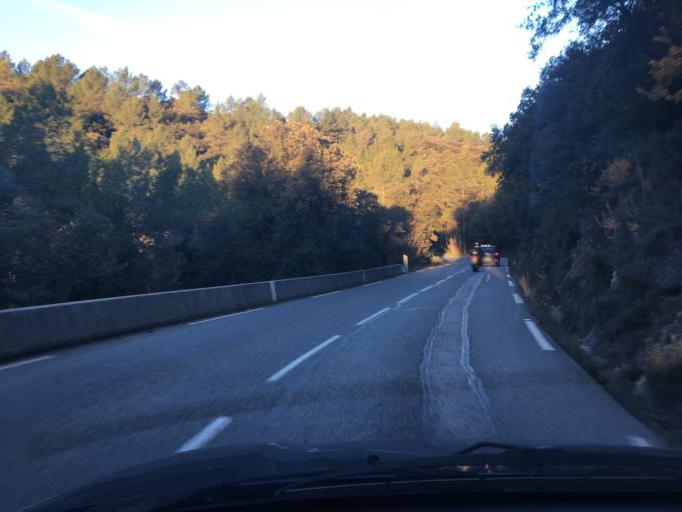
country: FR
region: Provence-Alpes-Cote d'Azur
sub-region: Departement du Var
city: Taradeau
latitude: 43.4576
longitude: 6.4205
